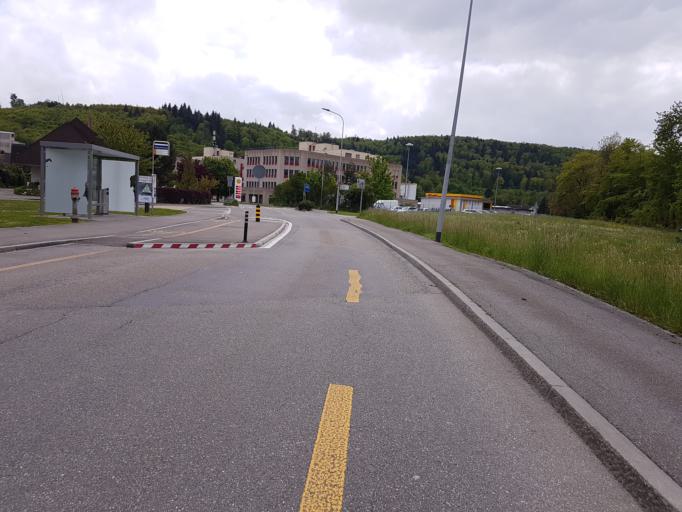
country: CH
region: Aargau
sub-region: Bezirk Brugg
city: Brugg
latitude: 47.4752
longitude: 8.1952
